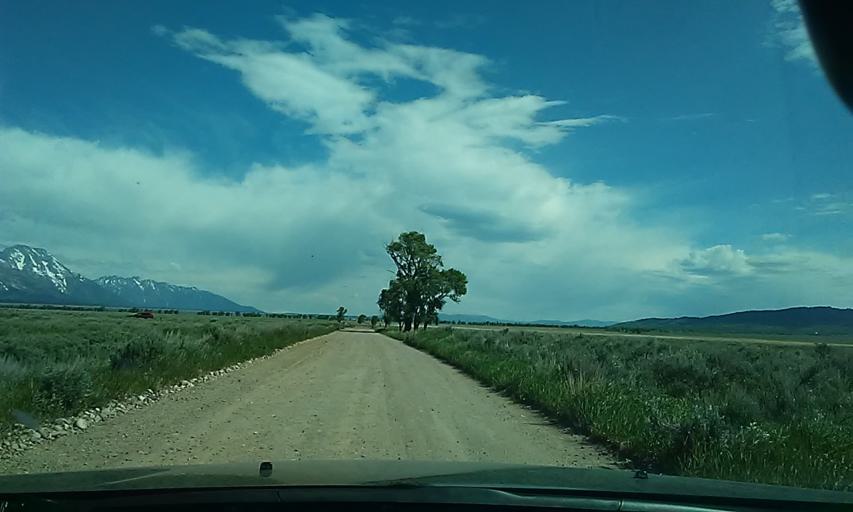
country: US
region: Wyoming
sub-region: Teton County
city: Jackson
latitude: 43.6295
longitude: -110.6641
